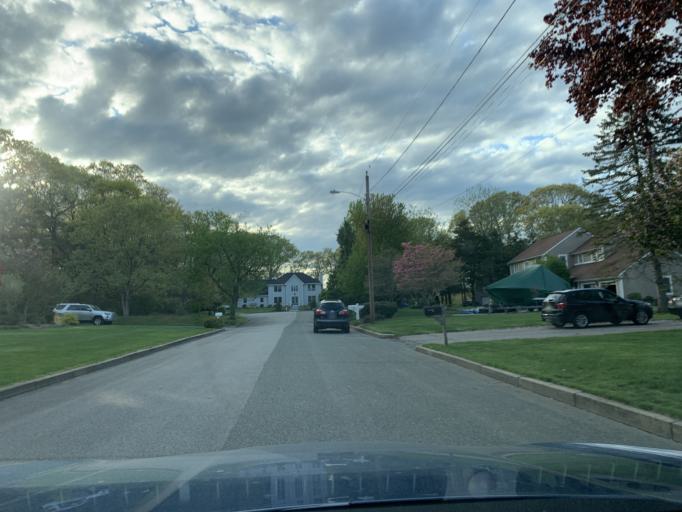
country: US
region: Rhode Island
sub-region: Kent County
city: East Greenwich
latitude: 41.6459
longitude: -71.4489
